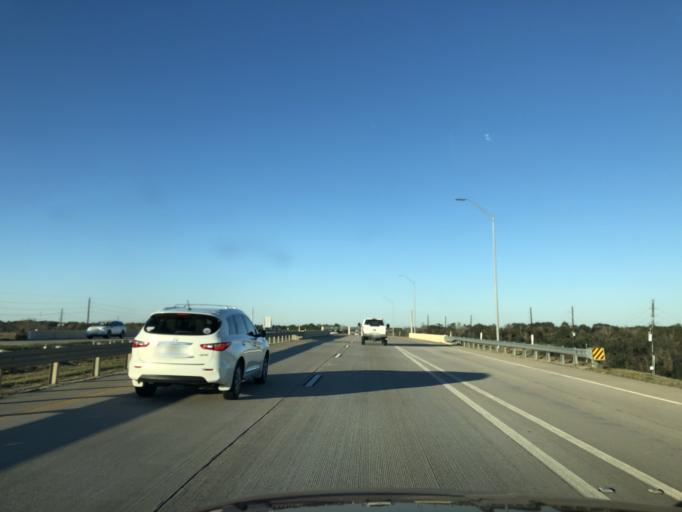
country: US
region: Texas
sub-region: Harris County
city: Cypress
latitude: 30.0194
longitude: -95.7679
